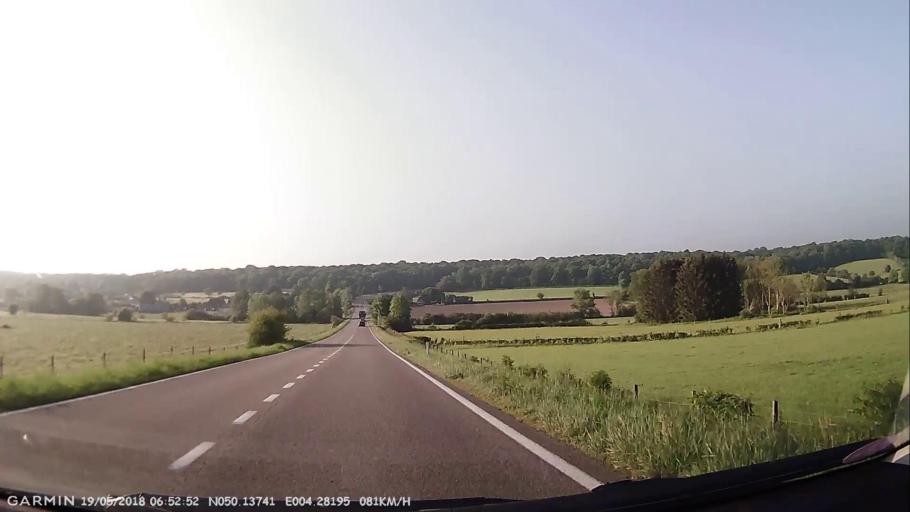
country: BE
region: Wallonia
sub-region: Province du Hainaut
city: Froidchapelle
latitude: 50.1374
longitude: 4.2818
